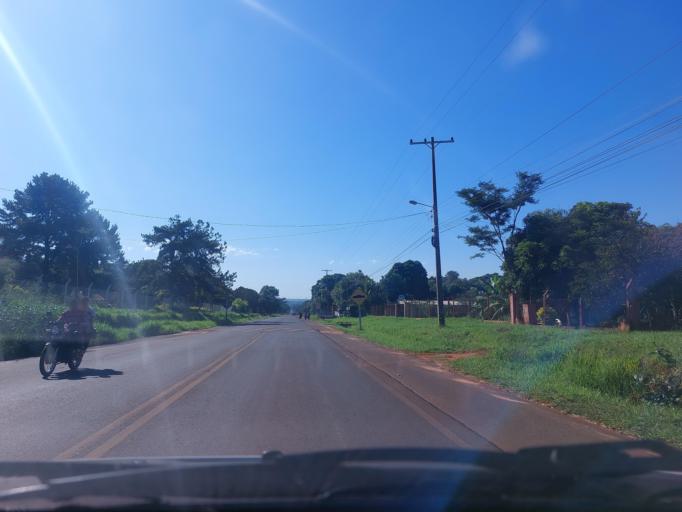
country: PY
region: San Pedro
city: Guayaybi
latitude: -24.5313
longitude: -56.4265
